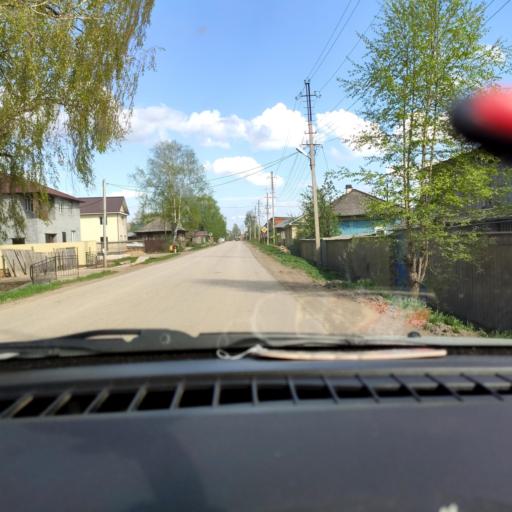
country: RU
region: Perm
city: Kudymkar
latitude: 59.0074
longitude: 54.6565
